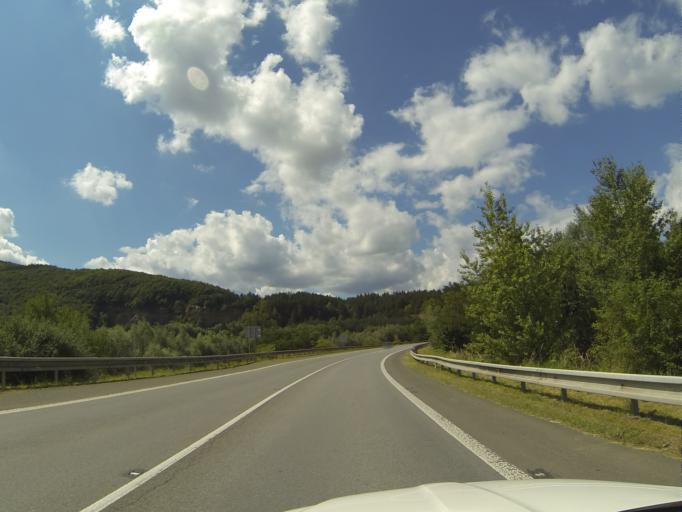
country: SK
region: Banskobystricky
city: Ziar nad Hronom
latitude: 48.5873
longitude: 18.8916
